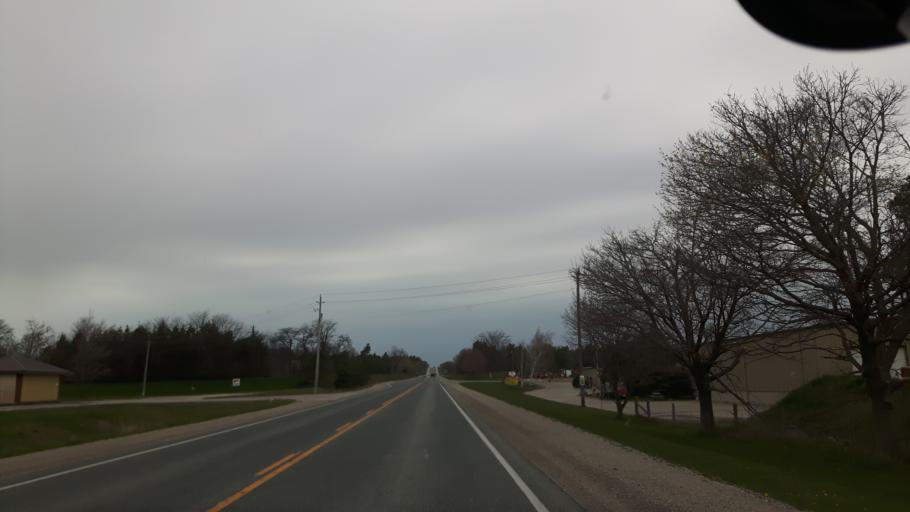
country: CA
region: Ontario
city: Goderich
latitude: 43.6426
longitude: -81.5952
